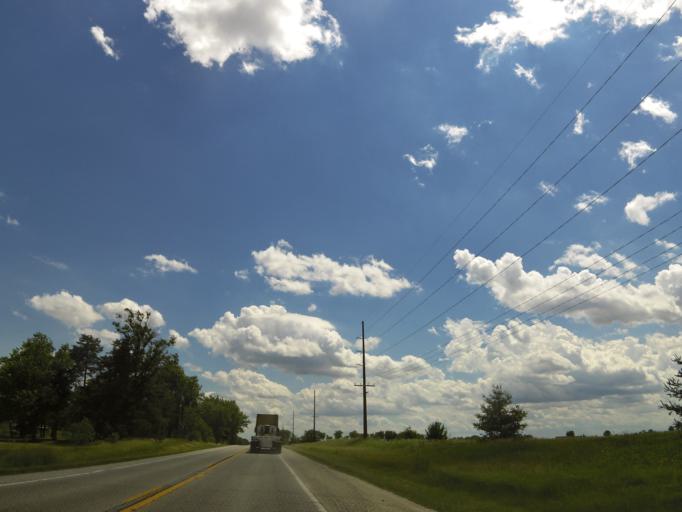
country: US
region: Iowa
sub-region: Buchanan County
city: Independence
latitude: 42.3973
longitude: -91.8899
